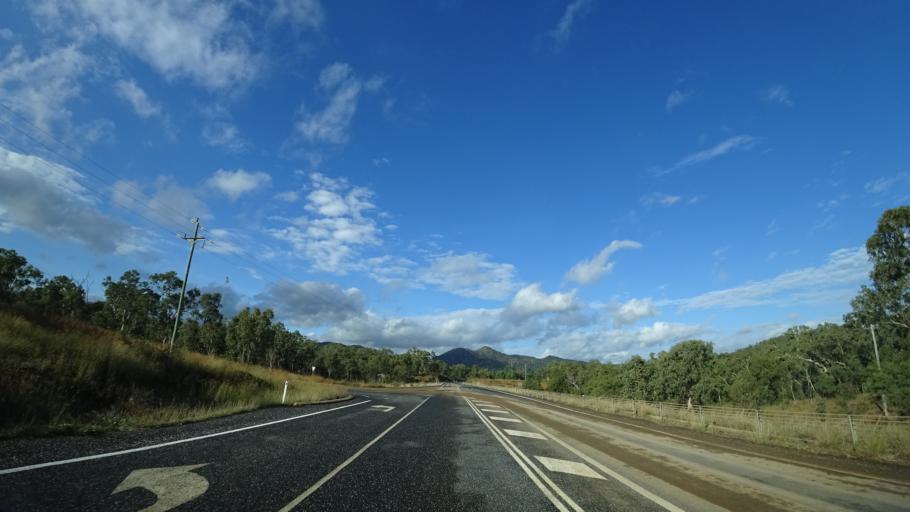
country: AU
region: Queensland
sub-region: Cook
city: Cooktown
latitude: -15.6134
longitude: 145.2212
